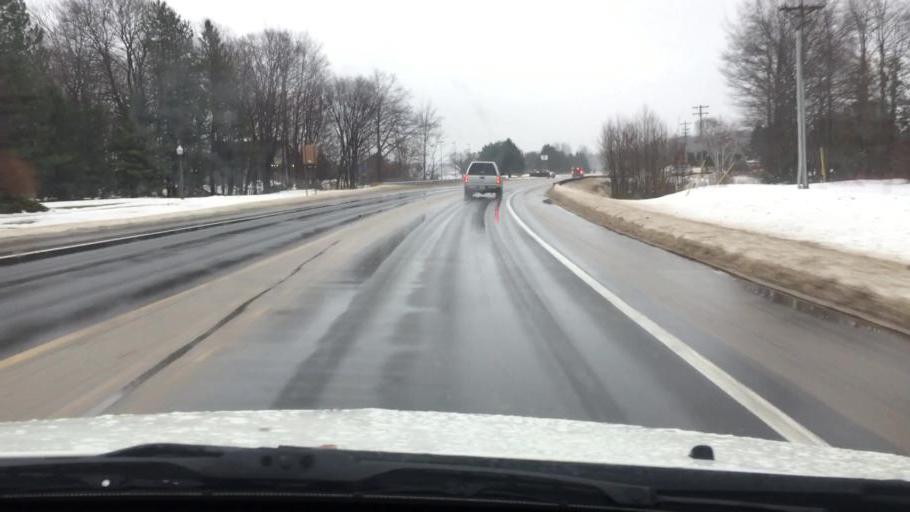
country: US
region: Michigan
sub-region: Charlevoix County
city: Charlevoix
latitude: 45.3015
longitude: -85.2577
